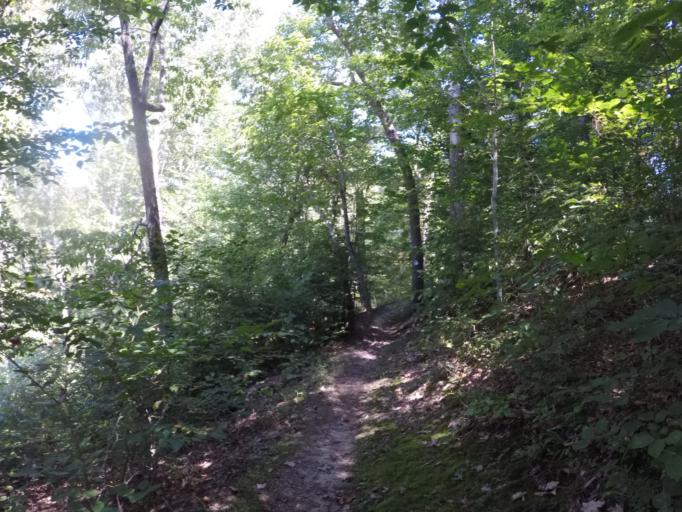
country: US
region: Ohio
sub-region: Lawrence County
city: Ironton
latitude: 38.6239
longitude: -82.6195
